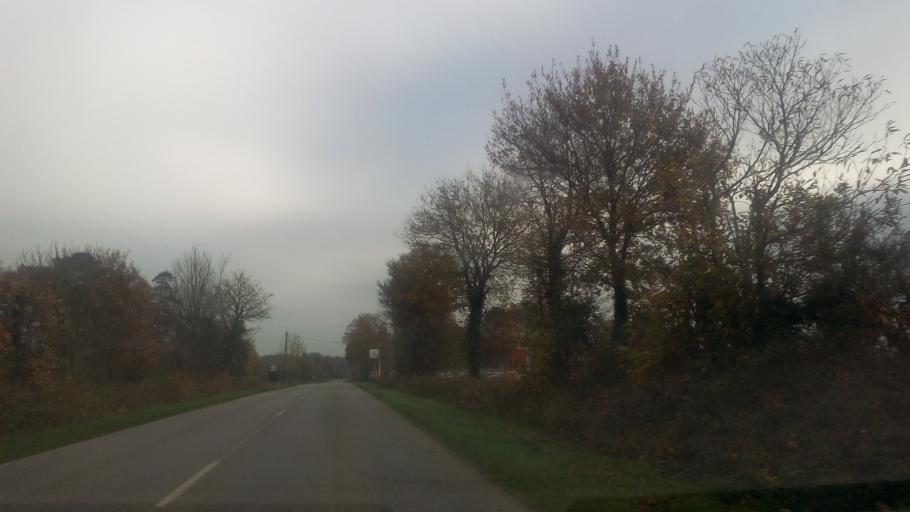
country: FR
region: Brittany
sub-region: Departement du Morbihan
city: Peillac
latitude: 47.7144
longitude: -2.1966
